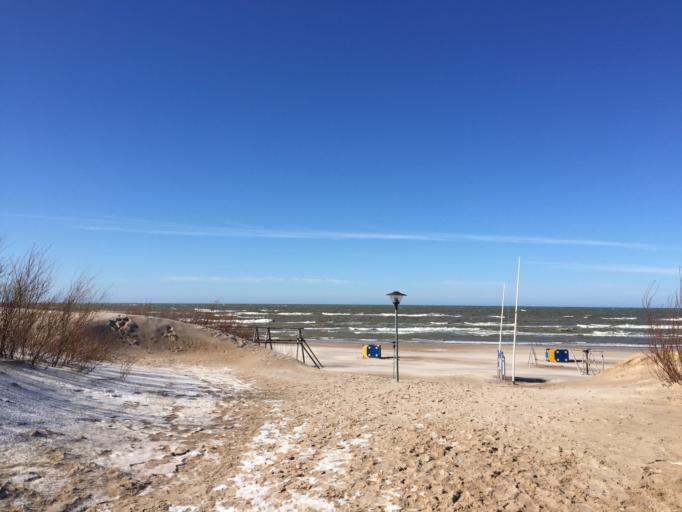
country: LV
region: Ventspils
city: Ventspils
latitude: 57.3920
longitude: 21.5309
